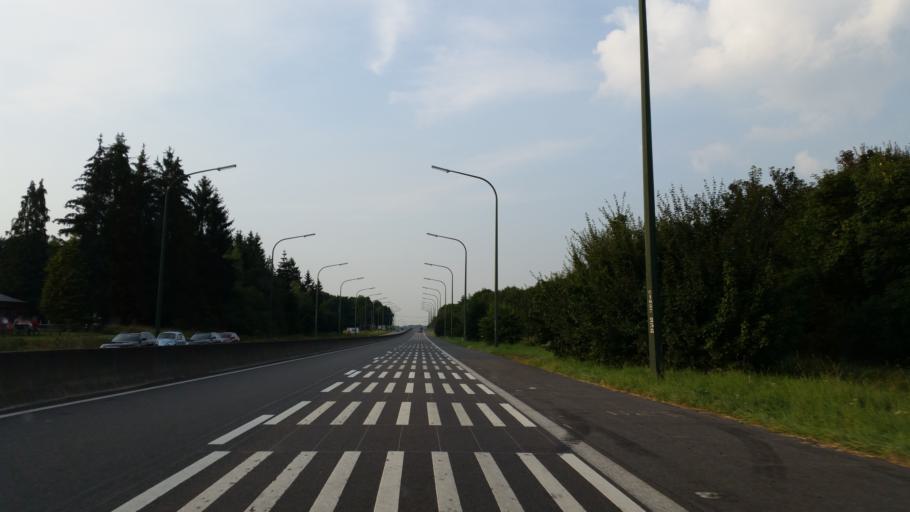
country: BE
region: Wallonia
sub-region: Province du Luxembourg
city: Marche-en-Famenne
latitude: 50.2720
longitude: 5.3476
